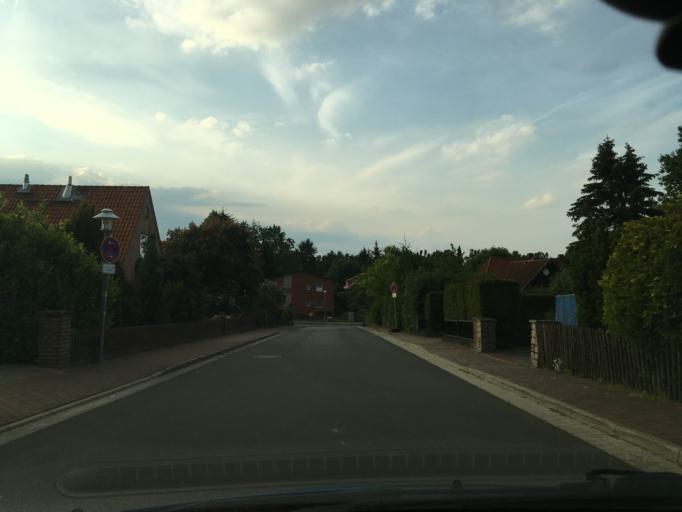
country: DE
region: Lower Saxony
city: Amelinghausen
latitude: 53.1326
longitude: 10.2103
